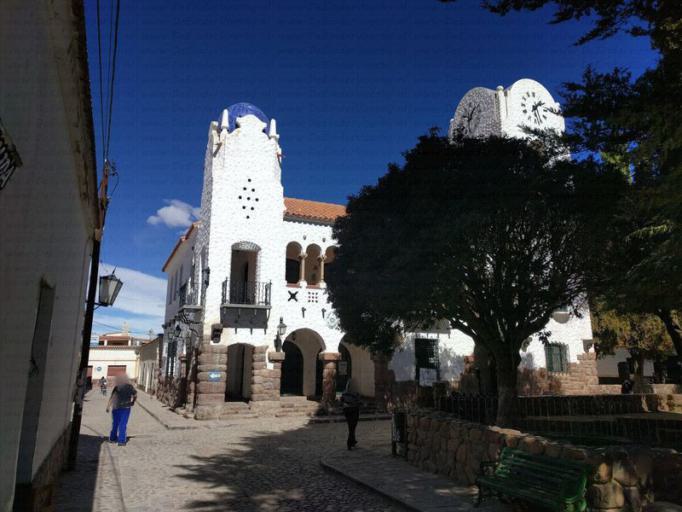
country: AR
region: Jujuy
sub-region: Departamento de Humahuaca
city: Humahuaca
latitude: -23.2038
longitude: -65.3488
